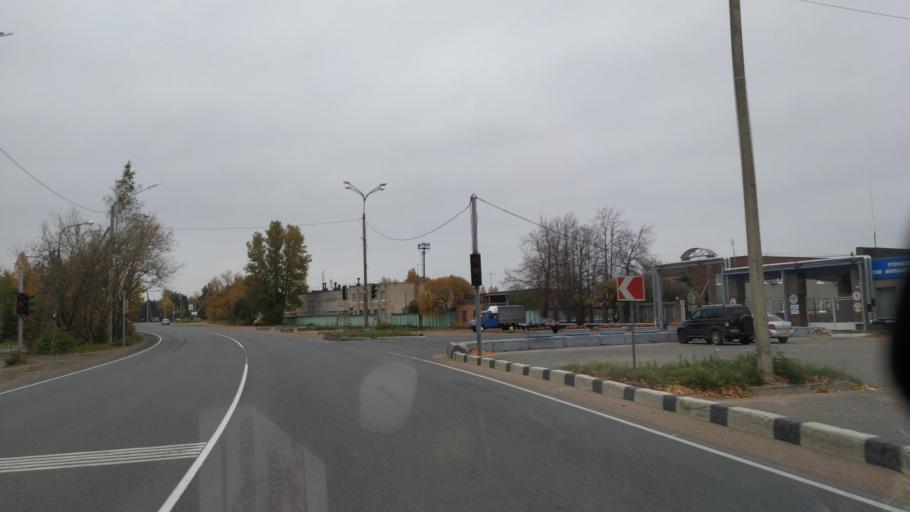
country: RU
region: Leningrad
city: Sosnovyy Bor
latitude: 59.8773
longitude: 29.0933
